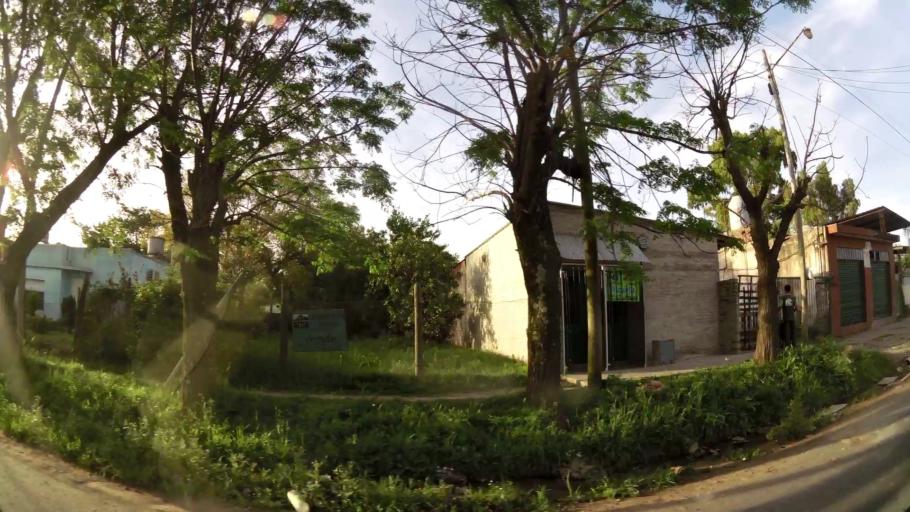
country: AR
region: Buenos Aires
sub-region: Partido de Almirante Brown
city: Adrogue
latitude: -34.7897
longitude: -58.3421
